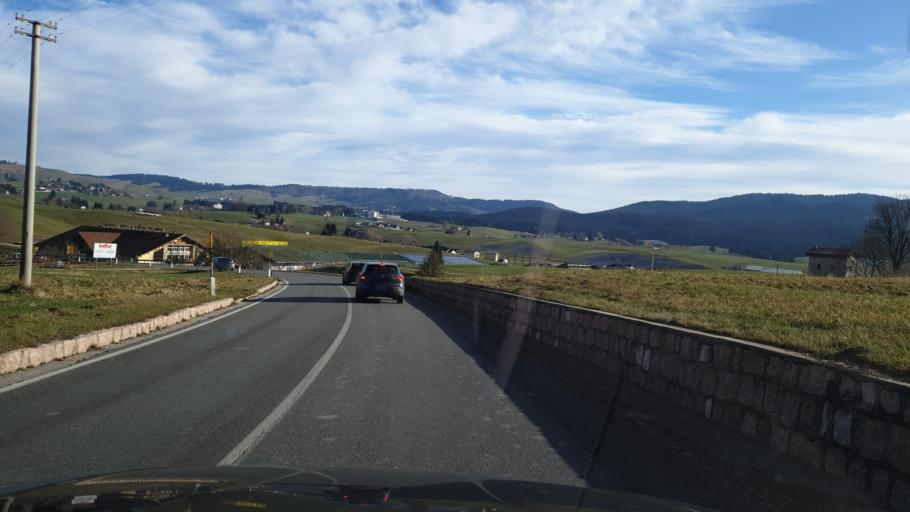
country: IT
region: Veneto
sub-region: Provincia di Vicenza
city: Canove di Roana
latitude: 45.8682
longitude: 11.4926
